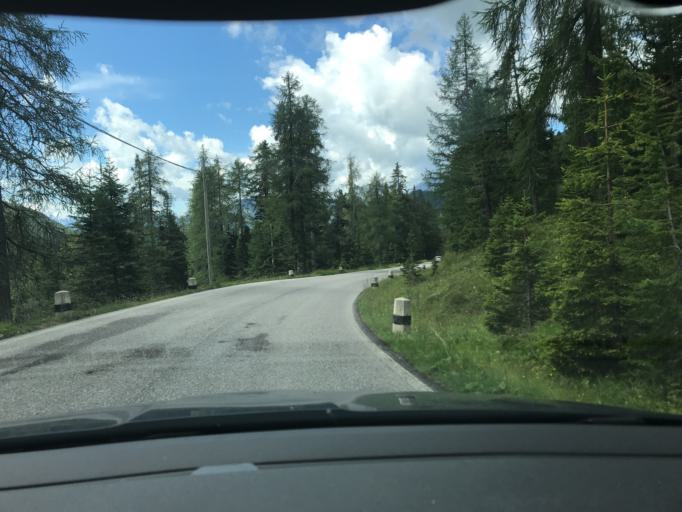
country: IT
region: Veneto
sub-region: Provincia di Belluno
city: Livinallongo del Col di Lana
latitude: 46.5130
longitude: 12.0006
